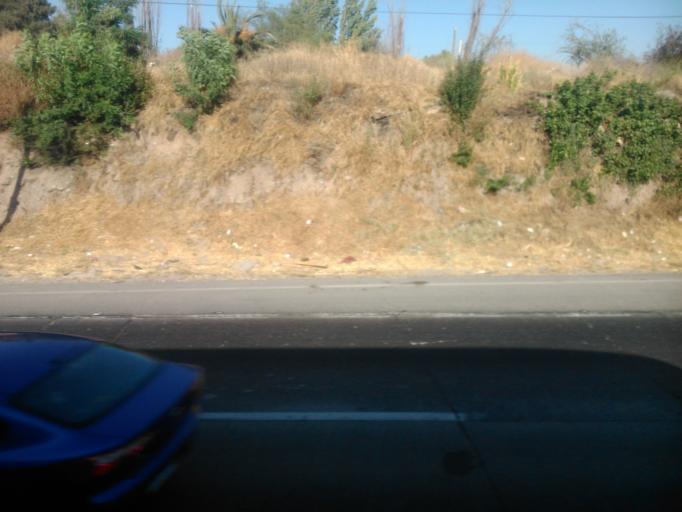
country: CL
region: Santiago Metropolitan
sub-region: Provincia de Maipo
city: Buin
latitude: -33.6953
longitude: -70.7220
